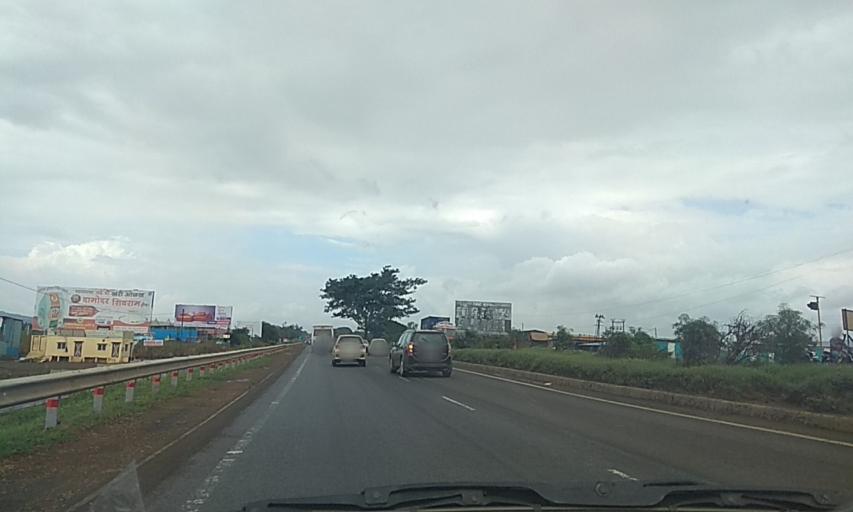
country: IN
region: Maharashtra
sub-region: Kolhapur
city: Kolhapur
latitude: 16.7213
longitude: 74.2829
